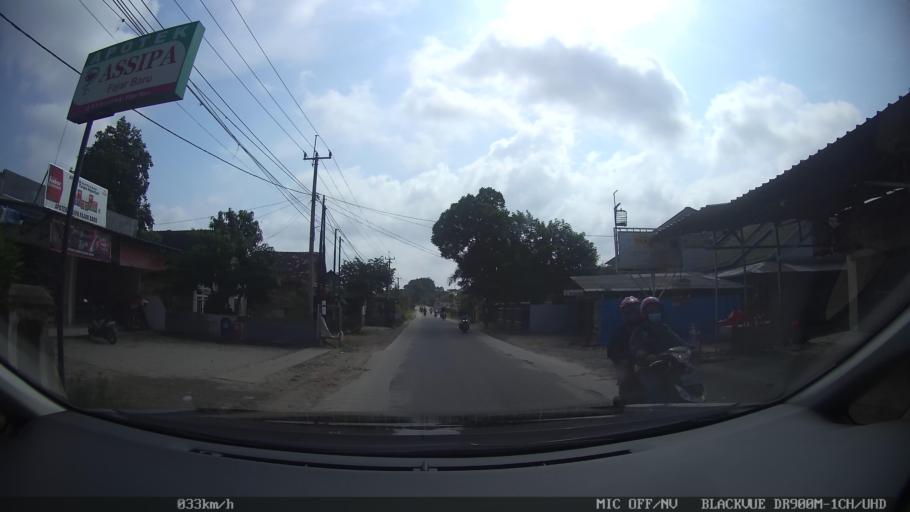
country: ID
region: Lampung
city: Kedaton
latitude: -5.3433
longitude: 105.2696
